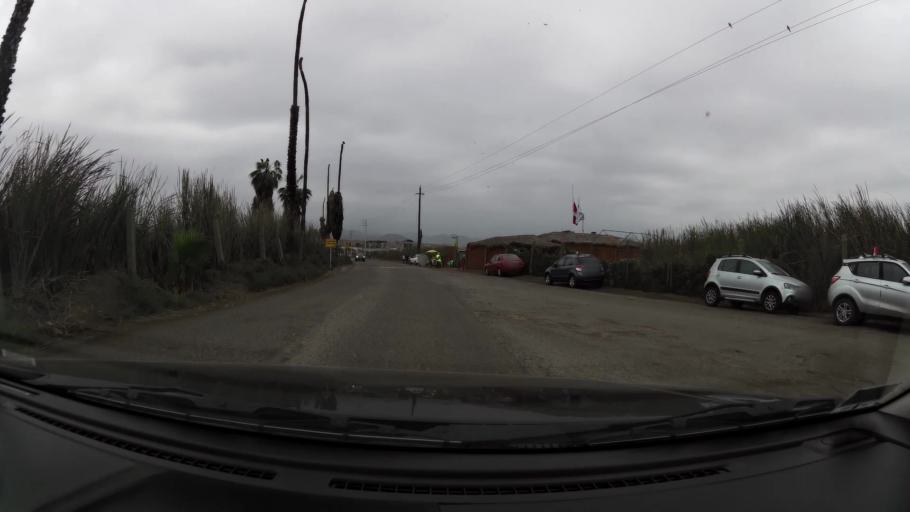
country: PE
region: Lima
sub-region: Lima
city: Surco
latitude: -12.2121
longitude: -76.9906
